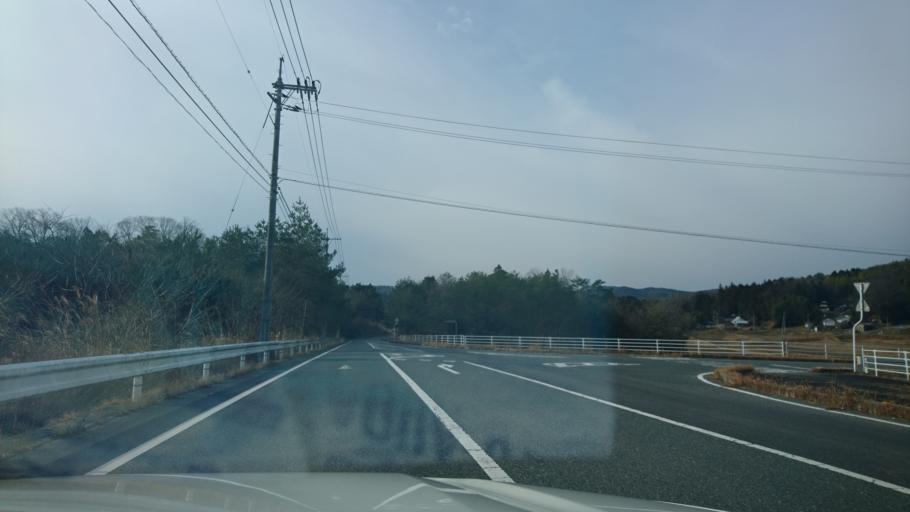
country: JP
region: Okayama
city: Takahashi
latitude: 34.8065
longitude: 133.6836
